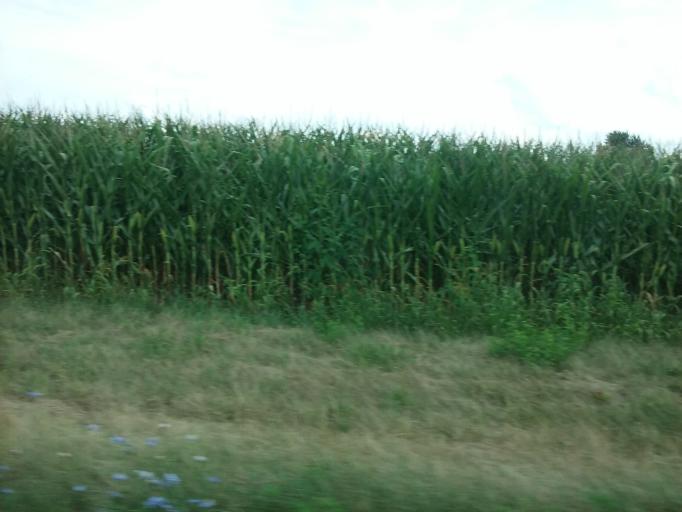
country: US
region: Ohio
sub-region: Hancock County
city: Findlay
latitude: 41.0419
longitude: -83.6887
